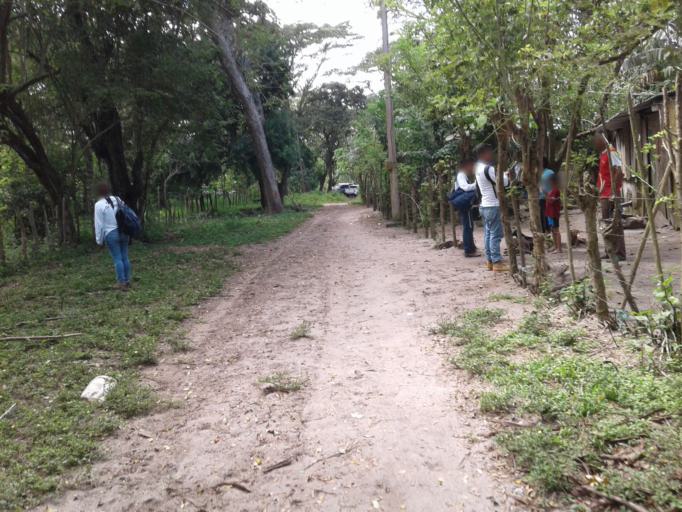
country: NI
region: Rivas
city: Cardenas
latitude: 11.1807
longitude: -85.4686
